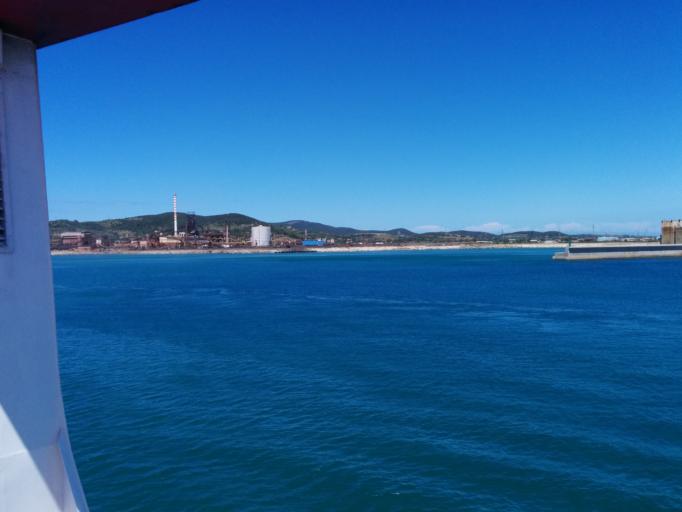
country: IT
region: Tuscany
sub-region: Provincia di Livorno
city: Piombino
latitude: 42.9322
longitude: 10.5654
